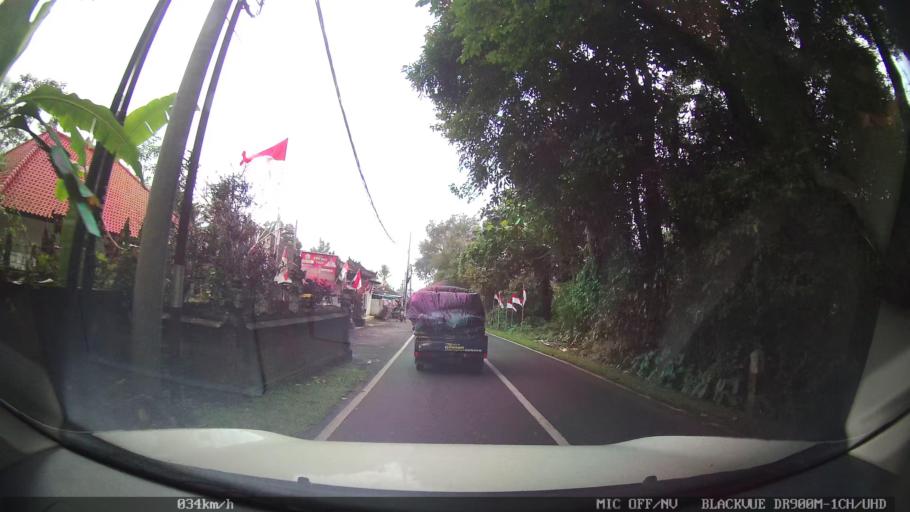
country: ID
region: Bali
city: Pohgending Kangin
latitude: -8.4308
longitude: 115.1434
